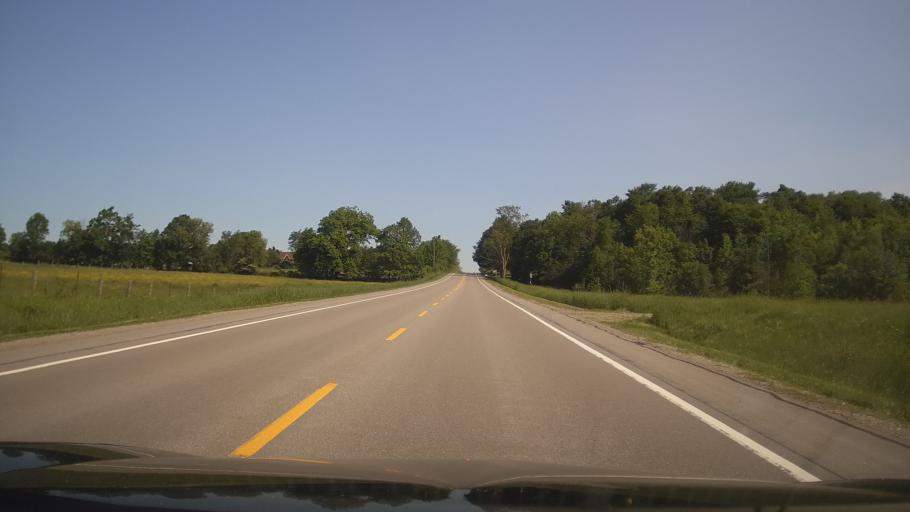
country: CA
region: Ontario
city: Omemee
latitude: 44.3966
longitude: -78.9079
